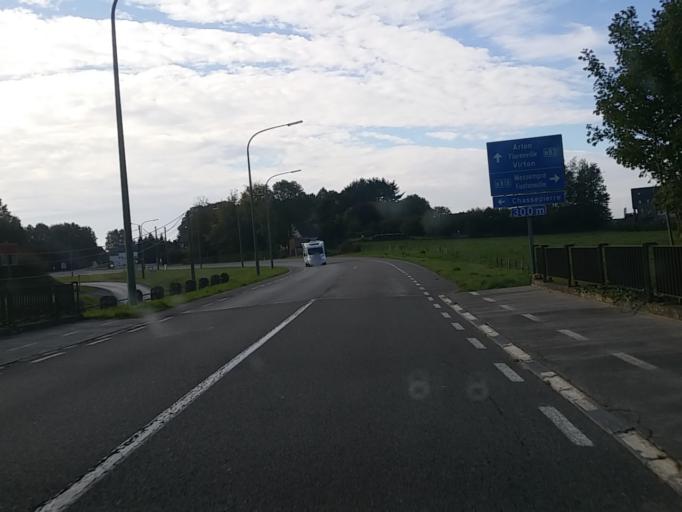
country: BE
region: Wallonia
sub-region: Province du Luxembourg
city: Florenville
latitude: 49.7031
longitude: 5.2581
